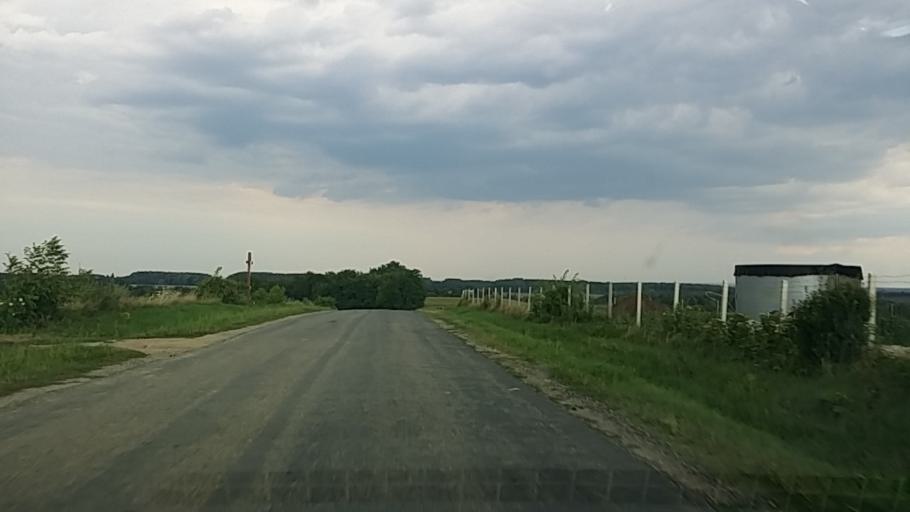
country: HU
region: Zala
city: Nagykanizsa
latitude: 46.4974
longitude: 17.0704
